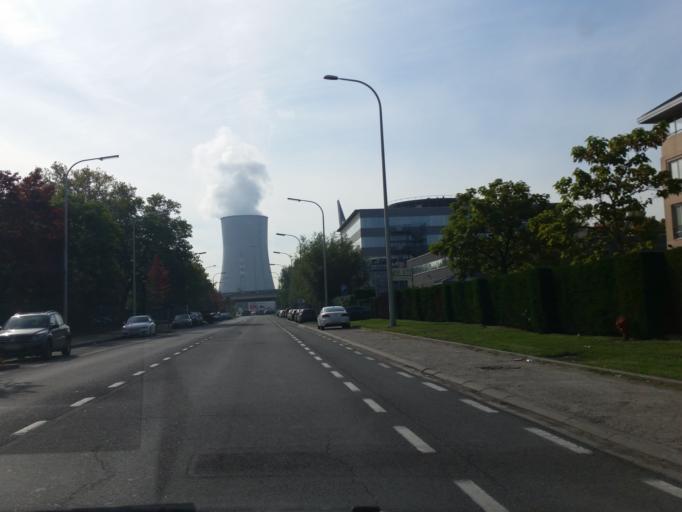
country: BE
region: Flanders
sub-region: Provincie Vlaams-Brabant
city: Drogenbos
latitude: 50.8091
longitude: 4.3044
